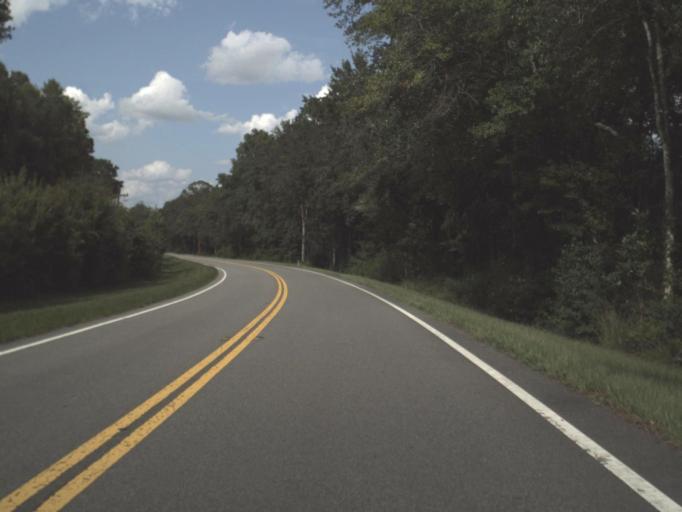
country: US
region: Florida
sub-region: Madison County
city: Madison
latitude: 30.4042
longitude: -83.6473
